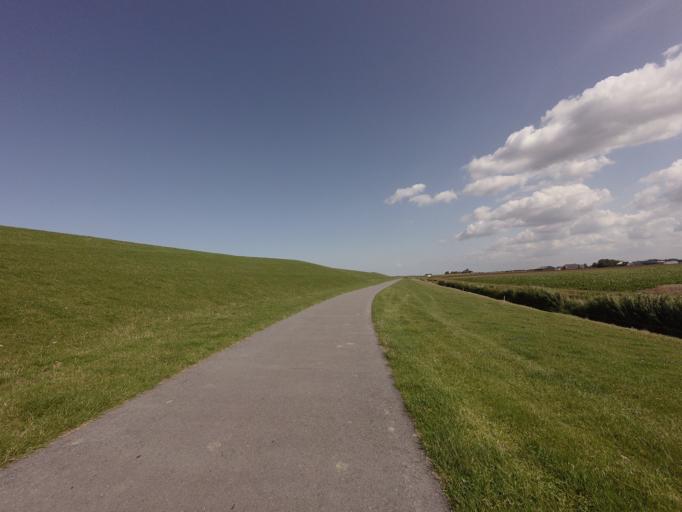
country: NL
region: Friesland
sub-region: Gemeente Dongeradeel
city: Holwerd
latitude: 53.3767
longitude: 5.8790
